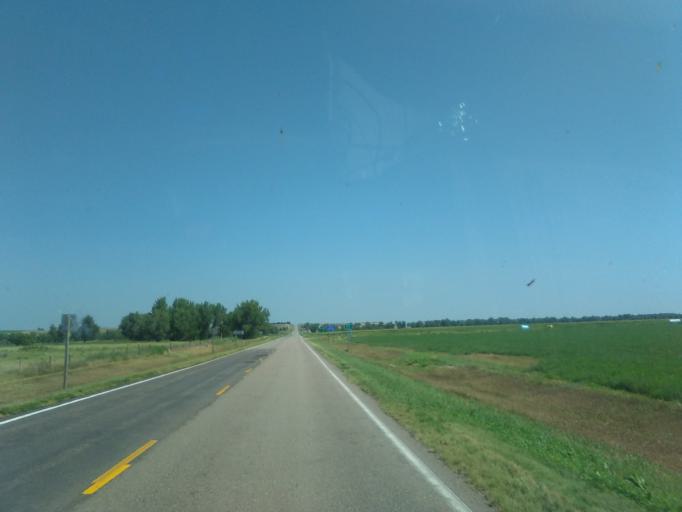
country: US
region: Nebraska
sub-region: Dundy County
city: Benkelman
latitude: 40.0010
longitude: -101.5423
